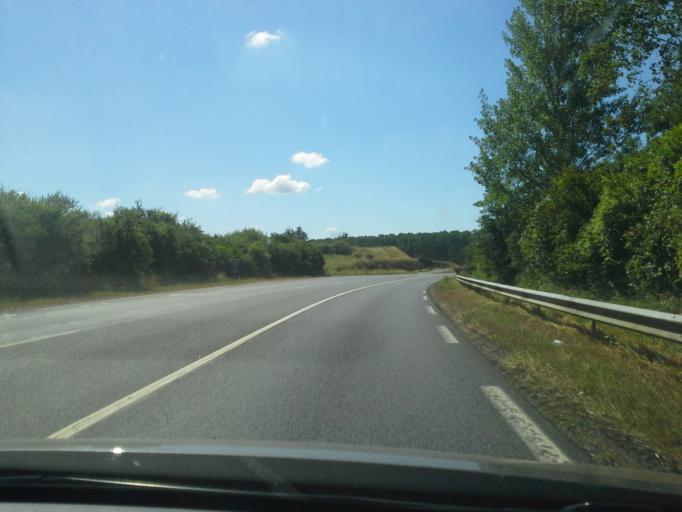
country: FR
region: Centre
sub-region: Departement du Loir-et-Cher
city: Saint-Sulpice-de-Pommeray
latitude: 47.6576
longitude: 1.2693
